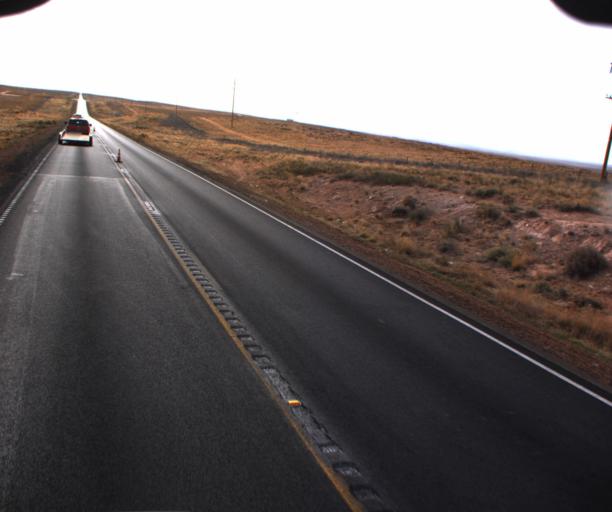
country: US
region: Arizona
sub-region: Apache County
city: Chinle
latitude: 36.0890
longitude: -109.6219
